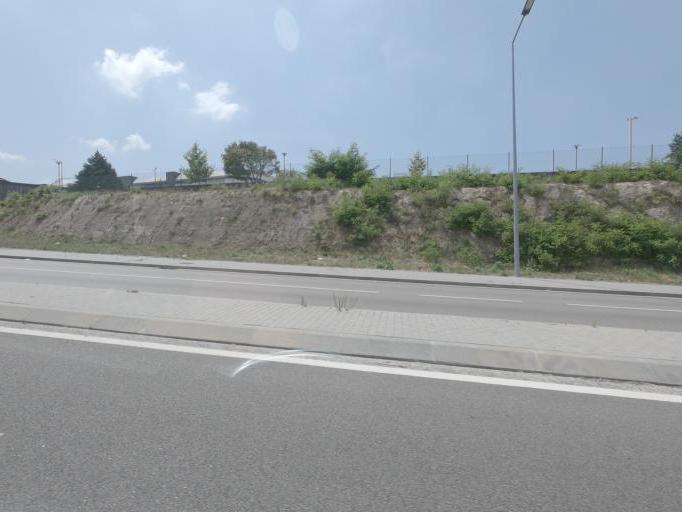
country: PT
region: Porto
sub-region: Paredes
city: Paredes
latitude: 41.1957
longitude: -8.3064
